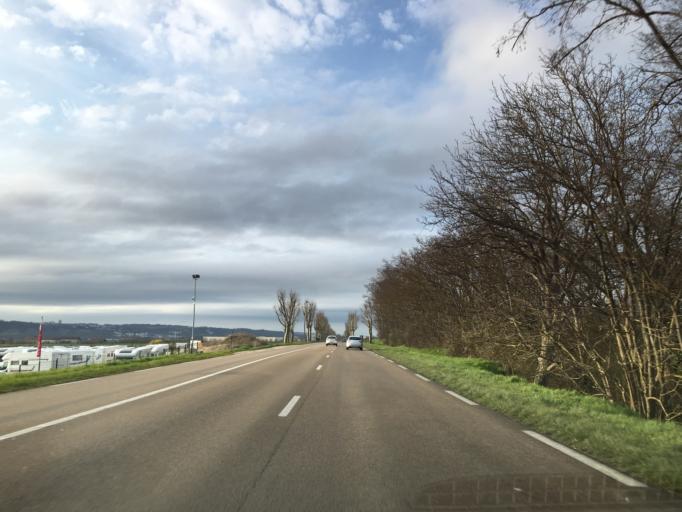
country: FR
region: Bourgogne
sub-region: Departement de l'Yonne
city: Maillot
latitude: 48.1620
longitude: 3.3019
